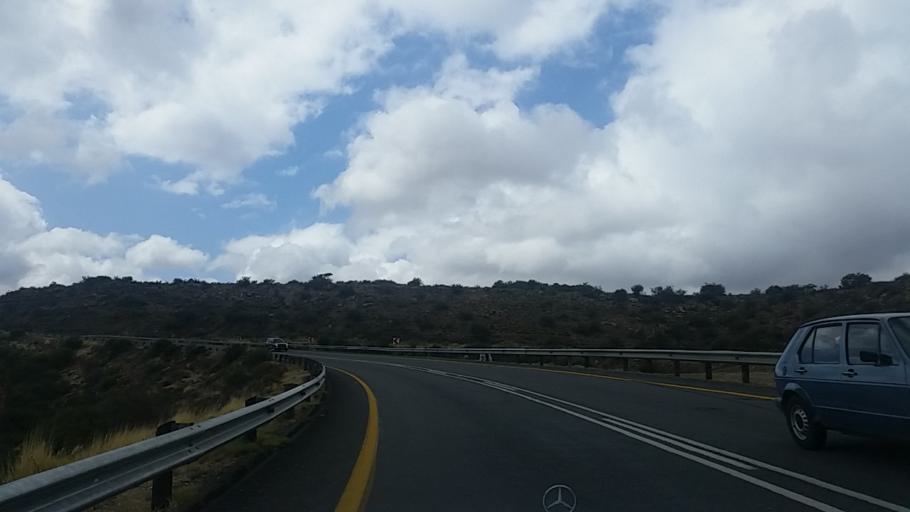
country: ZA
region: Eastern Cape
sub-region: Cacadu District Municipality
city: Graaff-Reinet
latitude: -32.1126
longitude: 24.6094
